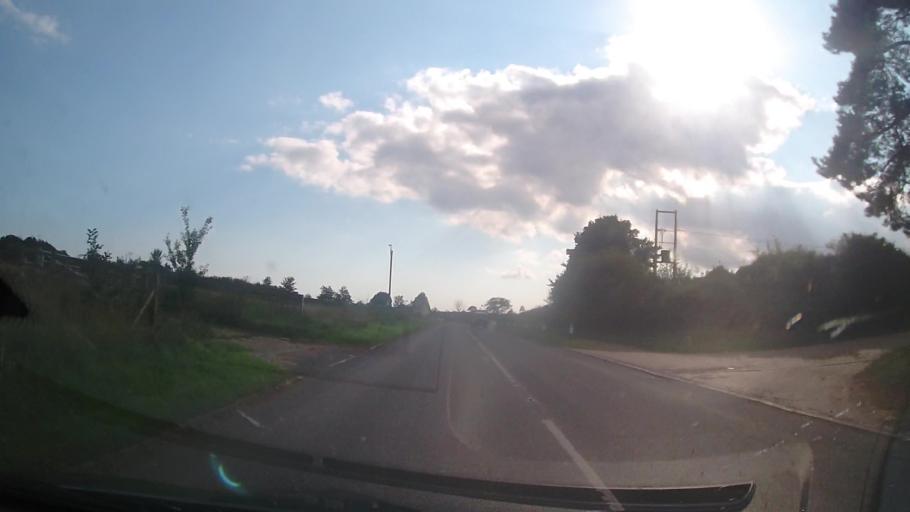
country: GB
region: England
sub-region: Kent
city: Hythe
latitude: 51.0953
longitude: 1.0618
